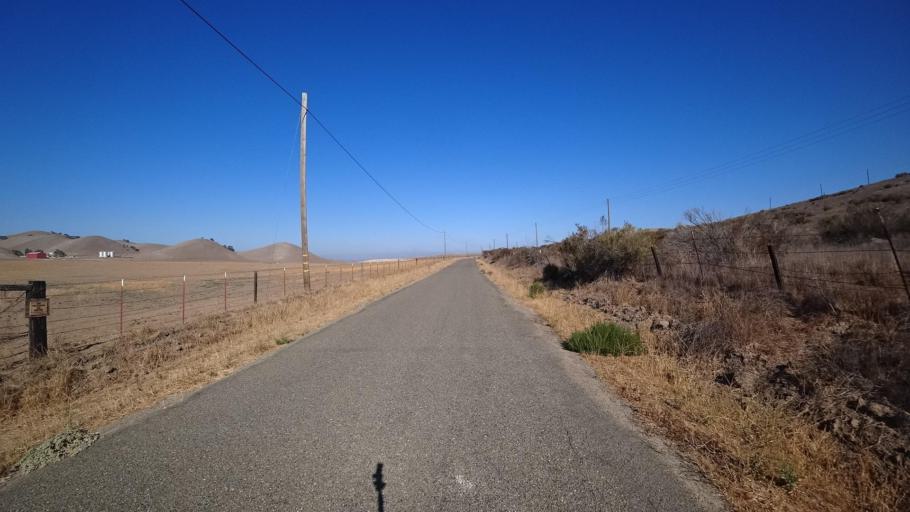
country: US
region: California
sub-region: Monterey County
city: King City
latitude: 36.0412
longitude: -120.9748
